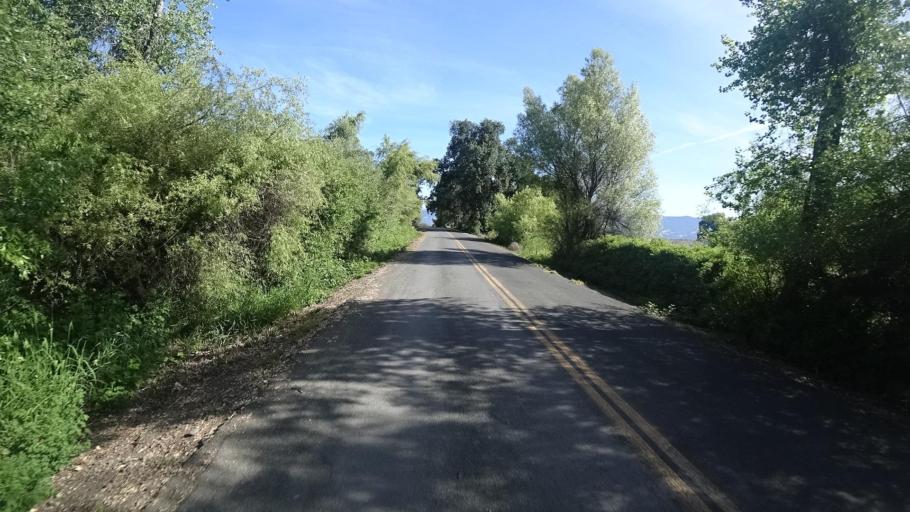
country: US
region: California
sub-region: Lake County
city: Kelseyville
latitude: 39.0258
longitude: -122.8475
